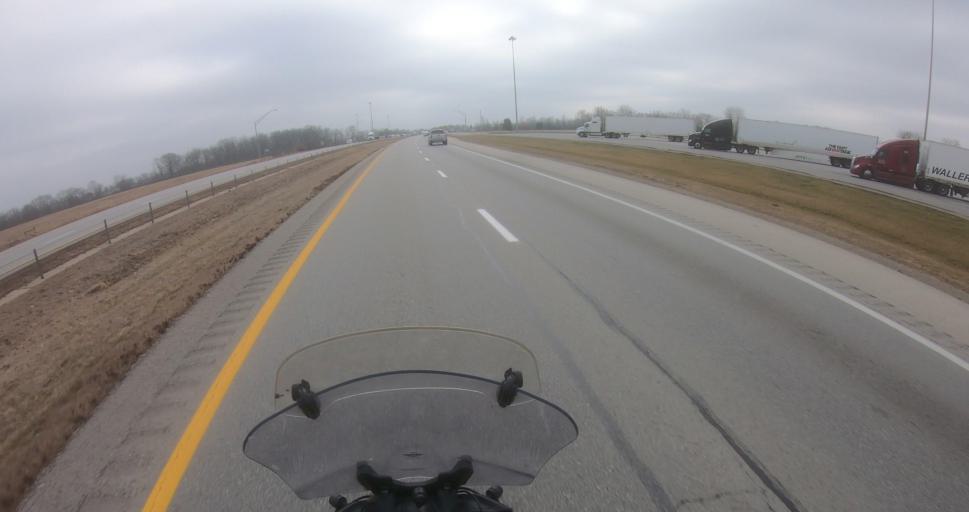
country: US
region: Ohio
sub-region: Miami County
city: Piqua
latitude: 40.1328
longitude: -84.2159
